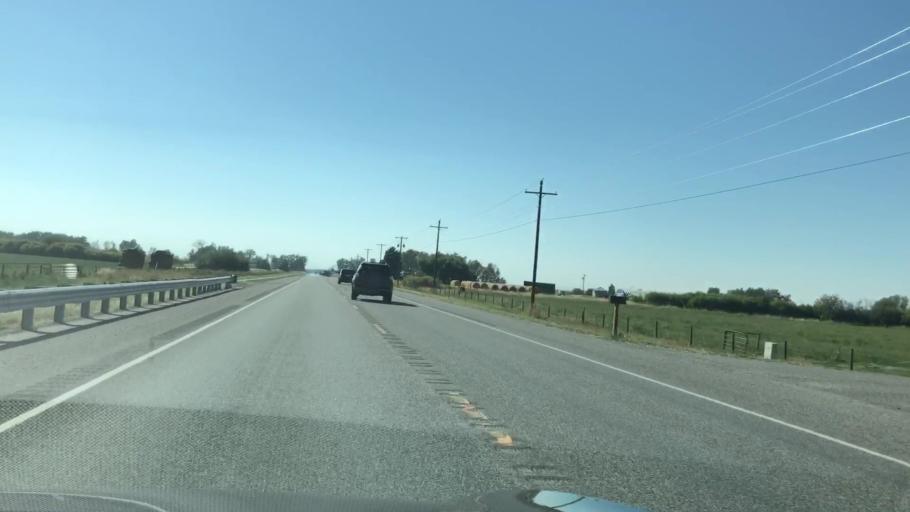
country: US
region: Montana
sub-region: Gallatin County
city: Belgrade
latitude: 45.7291
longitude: -111.1563
